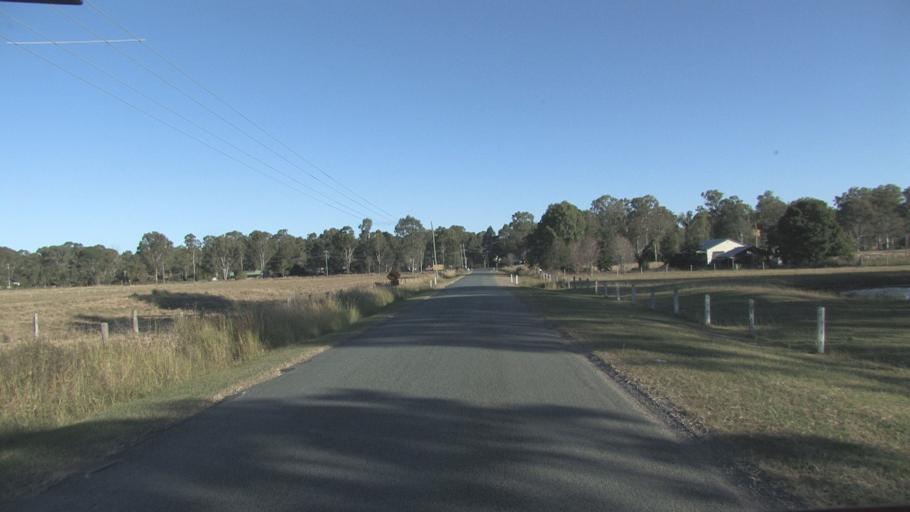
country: AU
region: Queensland
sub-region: Logan
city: Chambers Flat
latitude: -27.7812
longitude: 153.1354
